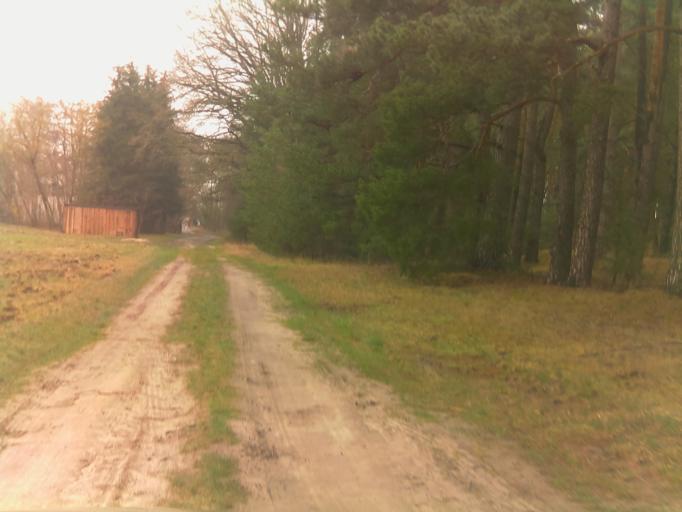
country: DE
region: Brandenburg
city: Schlepzig
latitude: 52.0186
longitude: 13.9852
